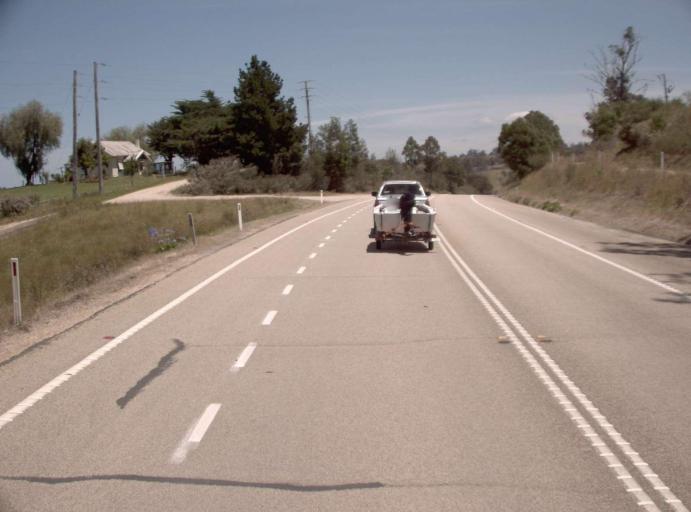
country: AU
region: Victoria
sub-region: East Gippsland
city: Bairnsdale
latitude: -37.7249
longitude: 147.8013
